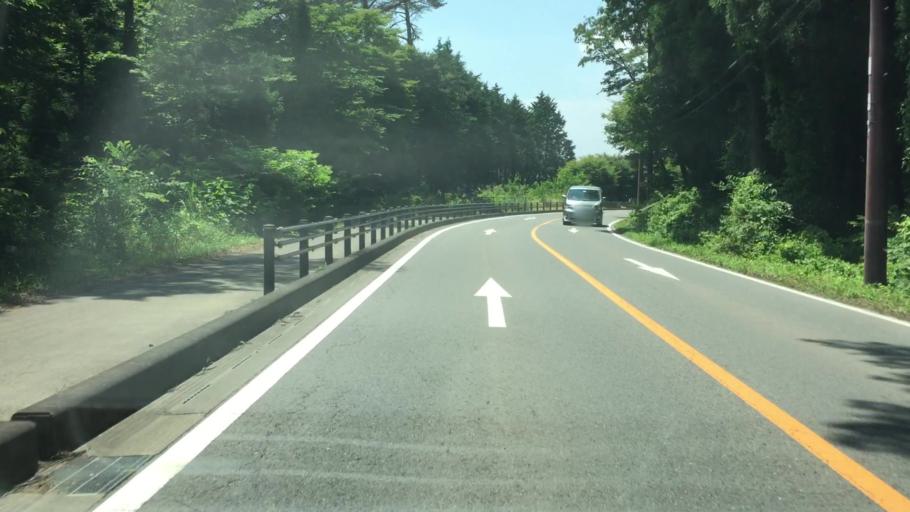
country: JP
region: Tochigi
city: Kuroiso
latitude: 37.0148
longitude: 139.9651
